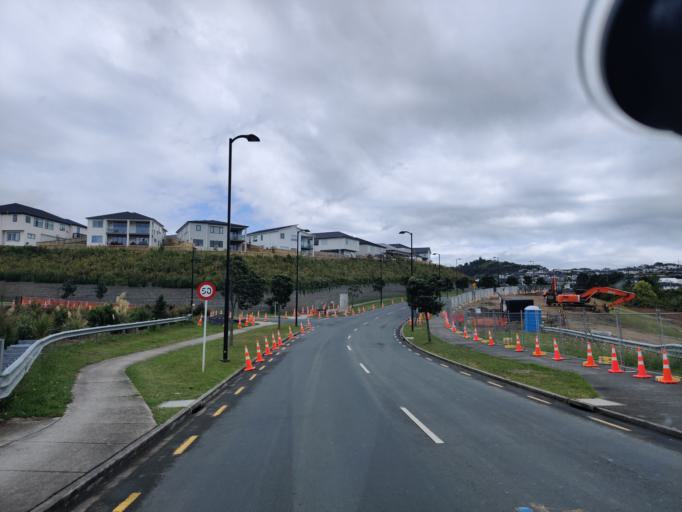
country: NZ
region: Auckland
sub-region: Auckland
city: Rothesay Bay
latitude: -36.5917
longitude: 174.6708
